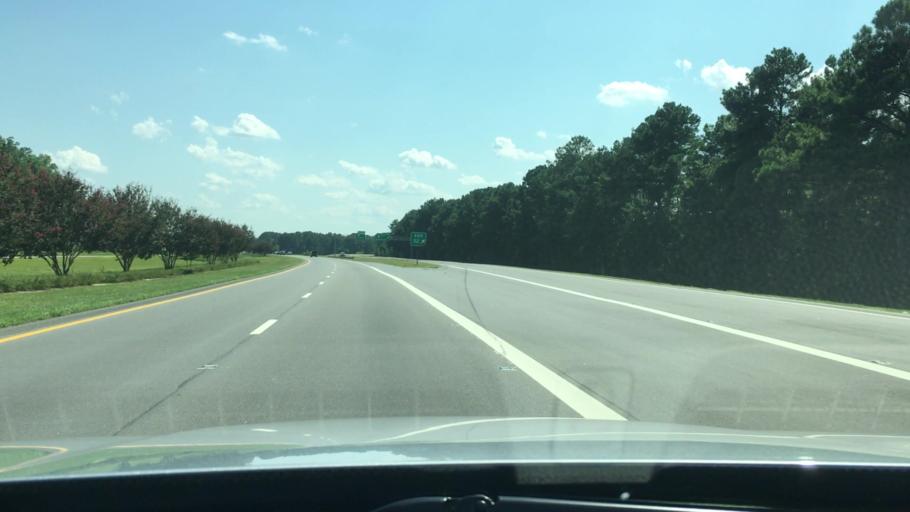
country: US
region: North Carolina
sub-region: Cumberland County
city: Vander
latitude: 35.0514
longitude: -78.8005
